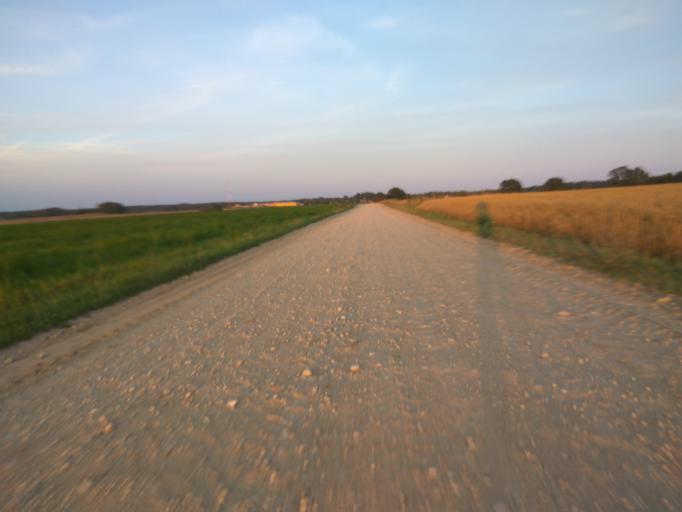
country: LV
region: Aizpute
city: Aizpute
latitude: 56.8379
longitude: 21.7421
